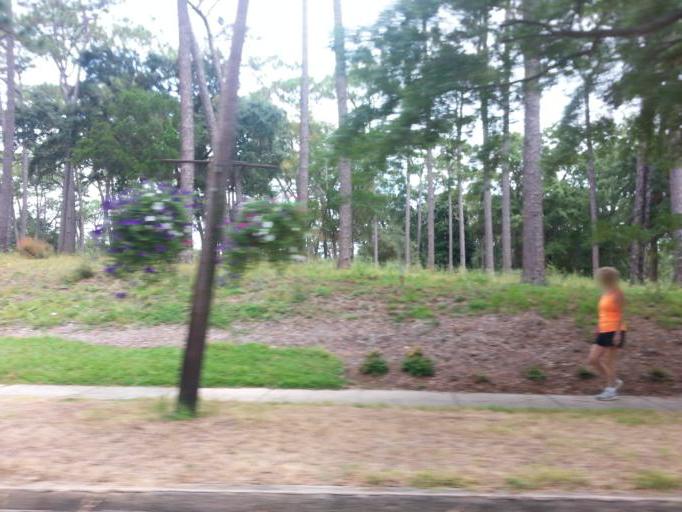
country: US
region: Alabama
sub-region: Baldwin County
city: Fairhope
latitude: 30.5231
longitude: -87.9091
